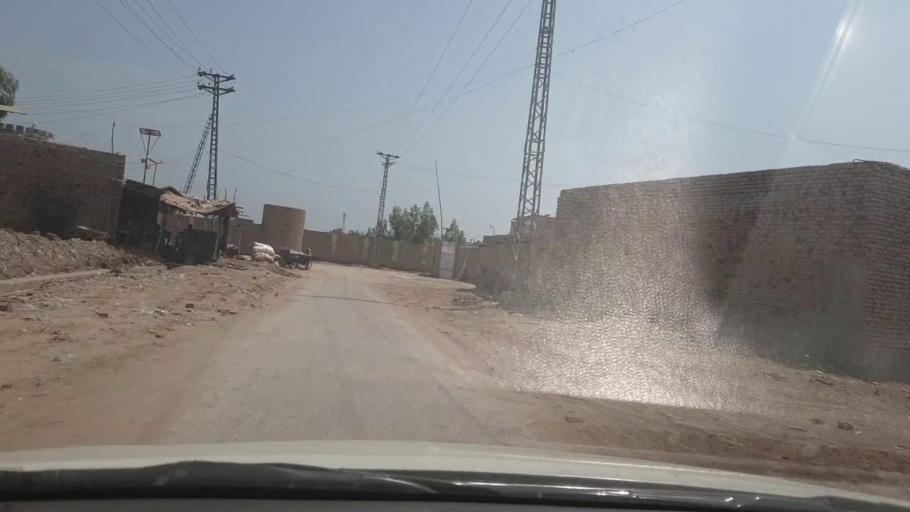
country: PK
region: Sindh
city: Garhi Yasin
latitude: 27.9113
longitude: 68.5112
